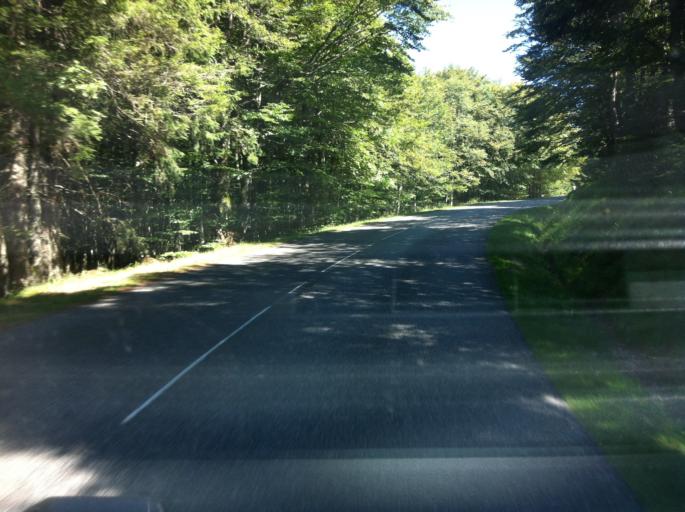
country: FR
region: Alsace
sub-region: Departement du Haut-Rhin
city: Soultzeren
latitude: 48.1010
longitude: 7.0545
